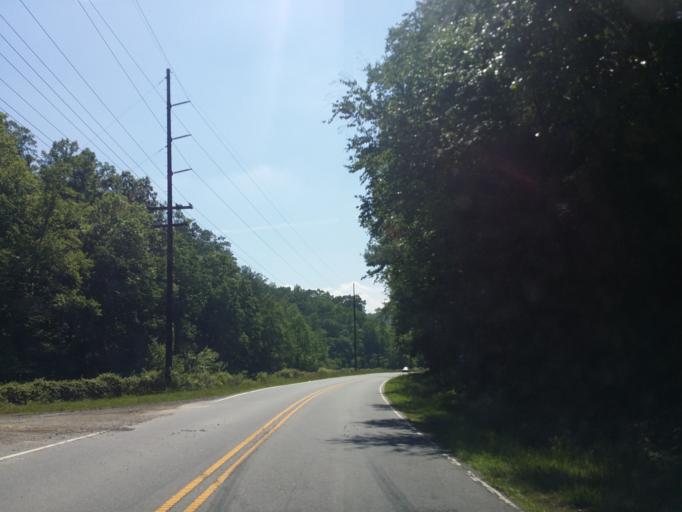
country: US
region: North Carolina
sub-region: Madison County
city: Marshall
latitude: 35.7069
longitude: -82.7693
